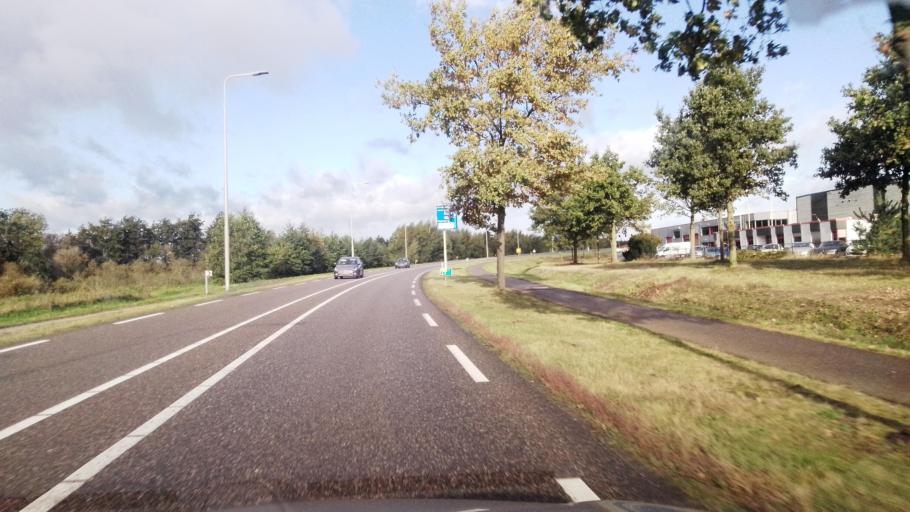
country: NL
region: Limburg
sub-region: Gemeente Peel en Maas
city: Maasbree
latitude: 51.3903
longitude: 6.0864
